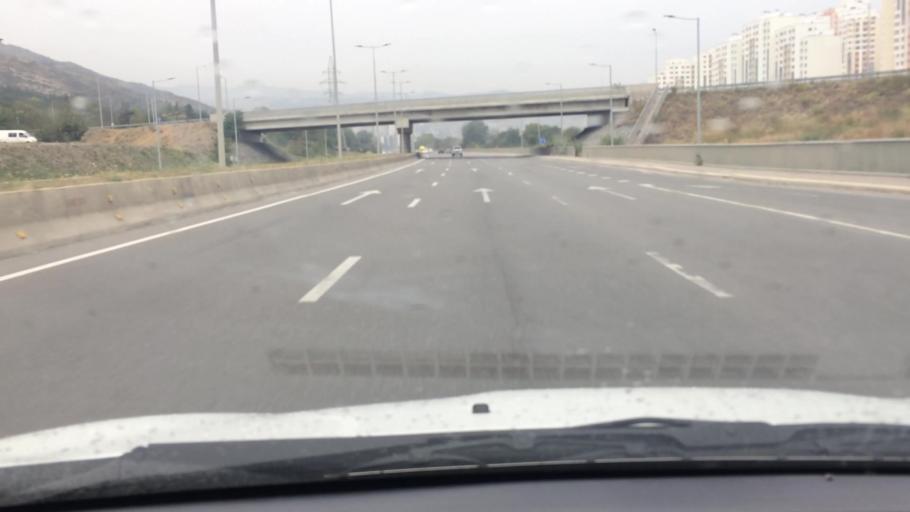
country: GE
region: T'bilisi
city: Tbilisi
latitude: 41.6693
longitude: 44.8599
